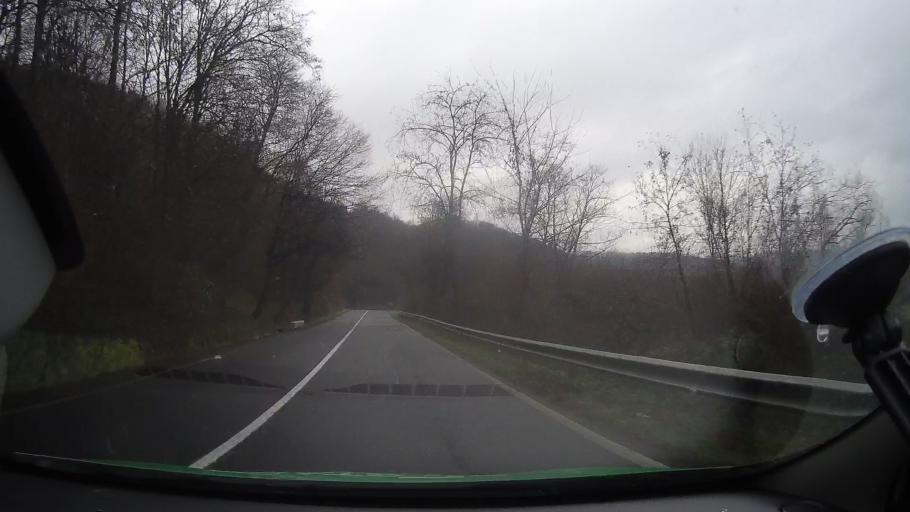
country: RO
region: Arad
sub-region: Comuna Gurahont
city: Gurahont
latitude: 46.2797
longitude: 22.3760
